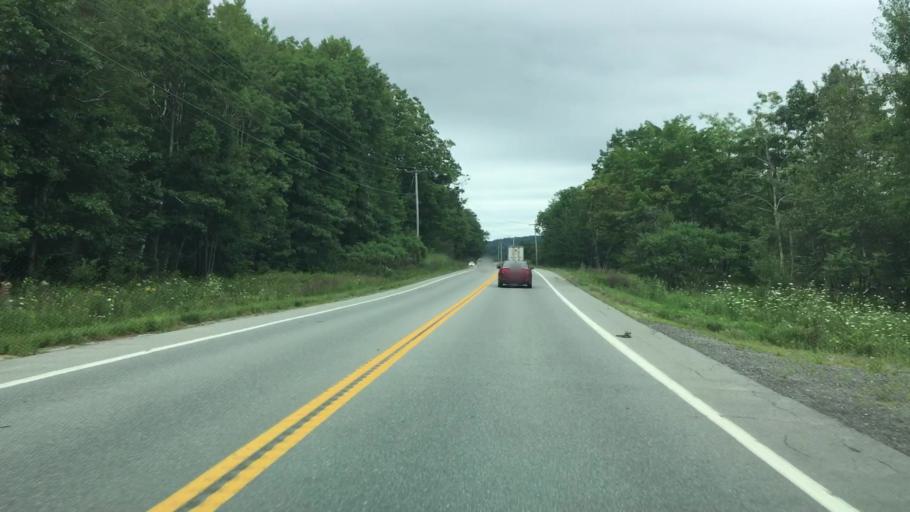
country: US
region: Maine
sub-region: Waldo County
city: Frankfort
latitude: 44.5808
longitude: -68.8628
